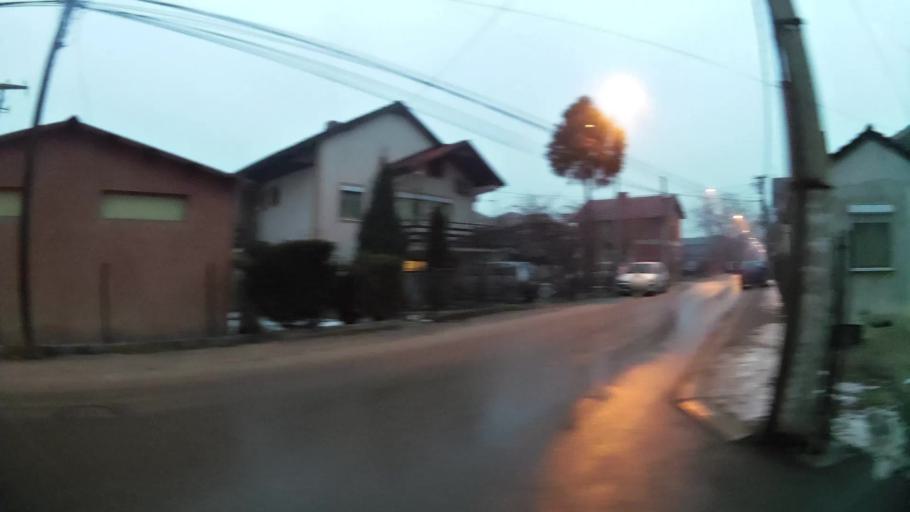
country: MK
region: Kisela Voda
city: Kisela Voda
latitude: 41.9766
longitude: 21.4926
